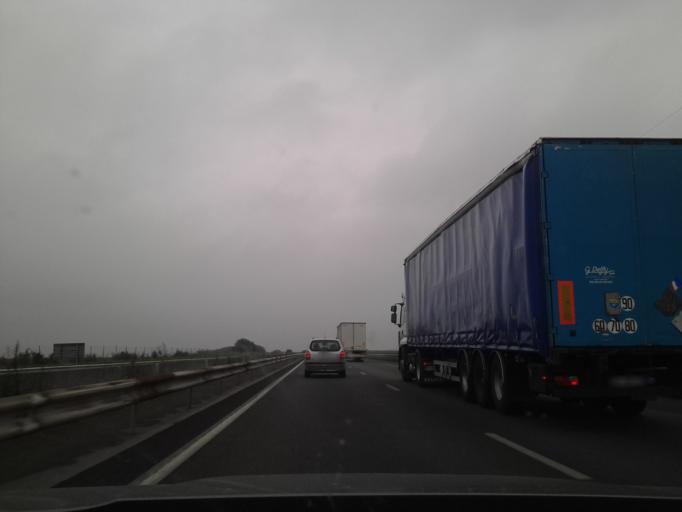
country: FR
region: Nord-Pas-de-Calais
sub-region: Departement du Nord
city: Iwuy
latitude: 50.2387
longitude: 3.2925
